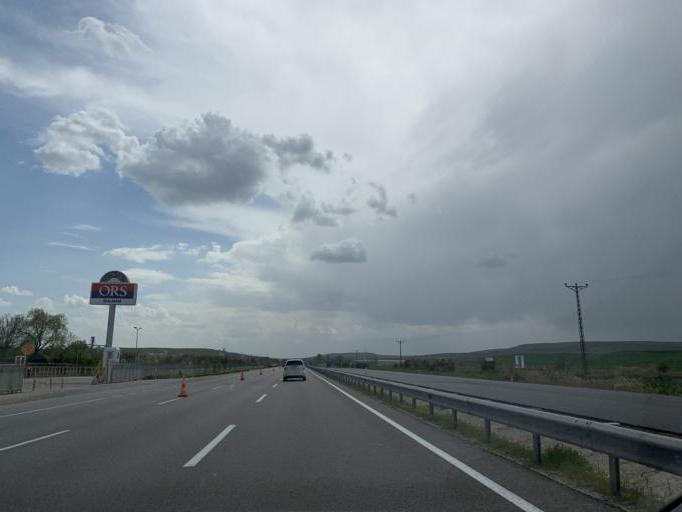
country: TR
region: Ankara
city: Polatli
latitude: 39.6470
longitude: 32.2107
